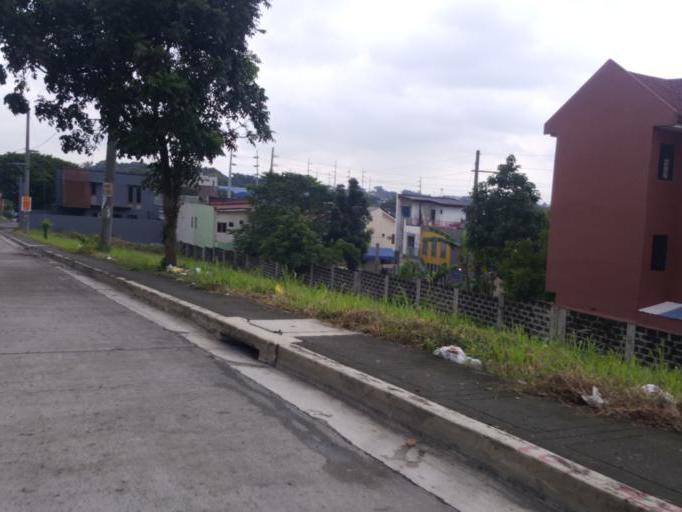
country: PH
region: Calabarzon
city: Bagong Pagasa
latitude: 14.7147
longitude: 121.0208
